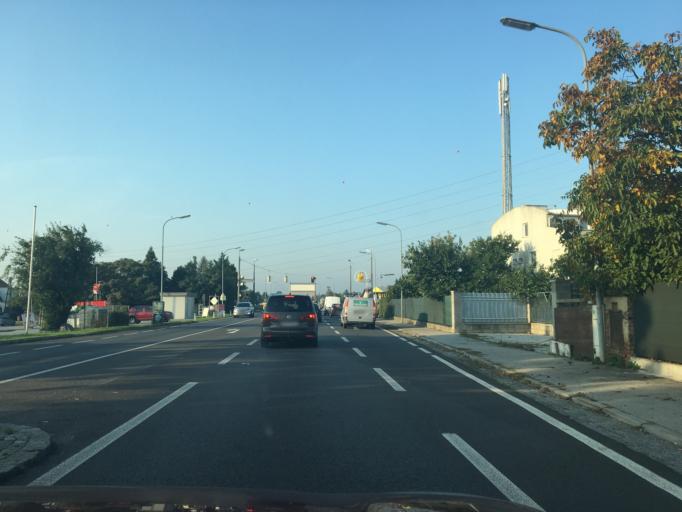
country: AT
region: Lower Austria
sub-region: Politischer Bezirk Wien-Umgebung
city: Gerasdorf bei Wien
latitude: 48.3240
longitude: 16.4453
